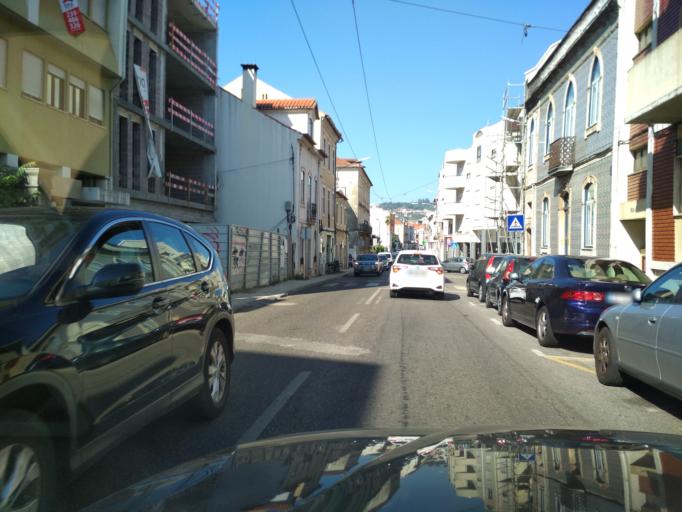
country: PT
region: Coimbra
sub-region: Coimbra
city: Coimbra
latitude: 40.2005
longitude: -8.4189
